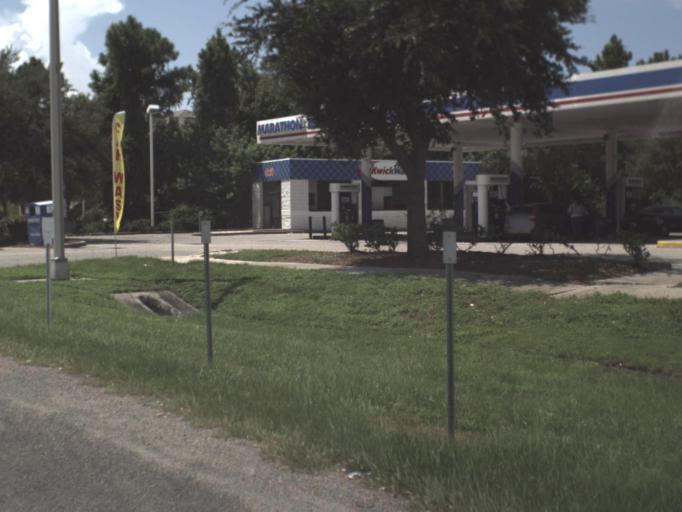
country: US
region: Florida
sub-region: Hillsborough County
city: Progress Village
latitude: 27.9223
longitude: -82.3500
